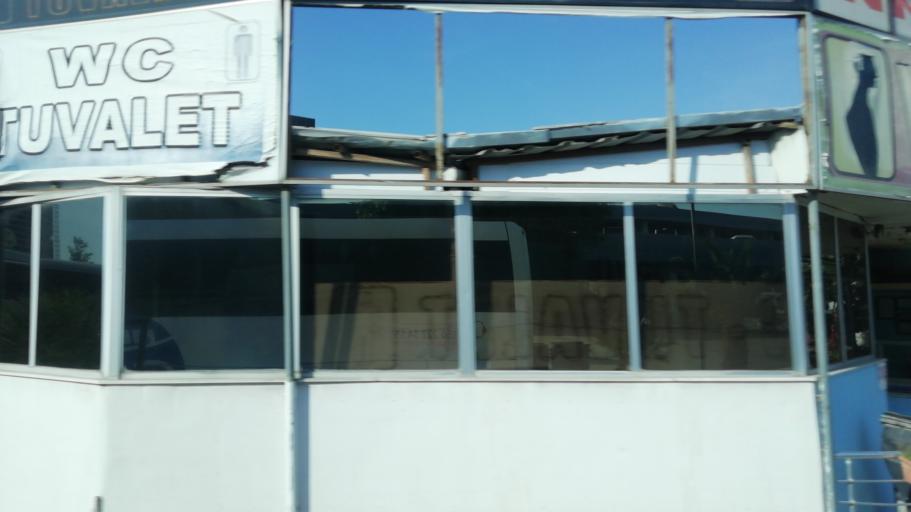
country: TR
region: Izmir
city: Bornova
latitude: 38.4321
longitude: 27.2147
